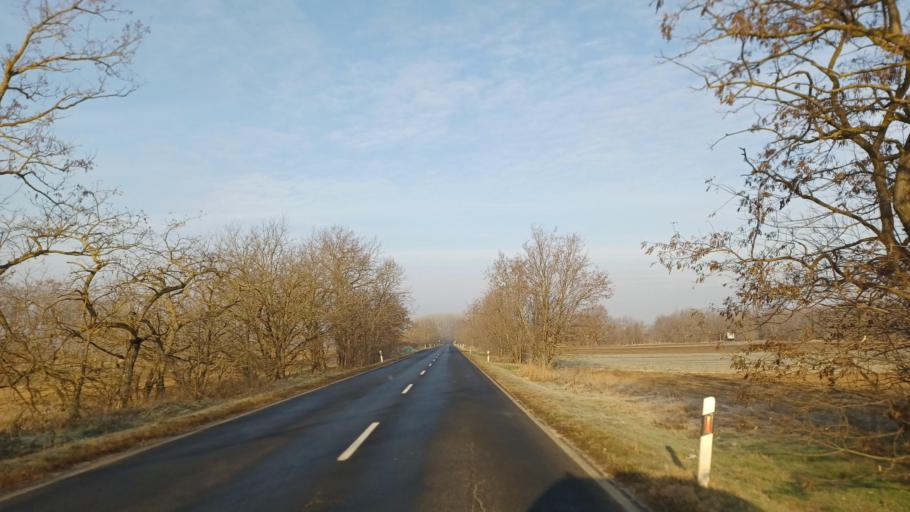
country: HU
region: Fejer
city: Cece
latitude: 46.7415
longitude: 18.6519
